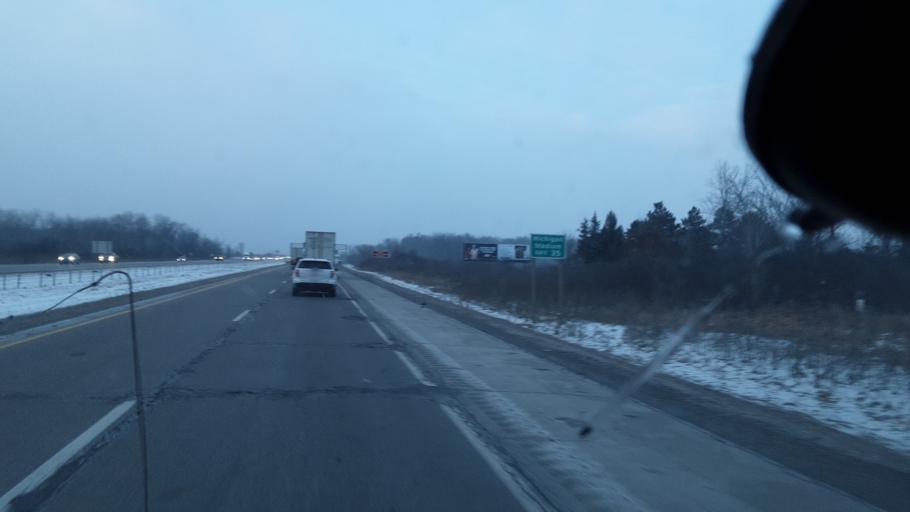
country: US
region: Michigan
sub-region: Washtenaw County
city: Ypsilanti
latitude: 42.2167
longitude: -83.6839
